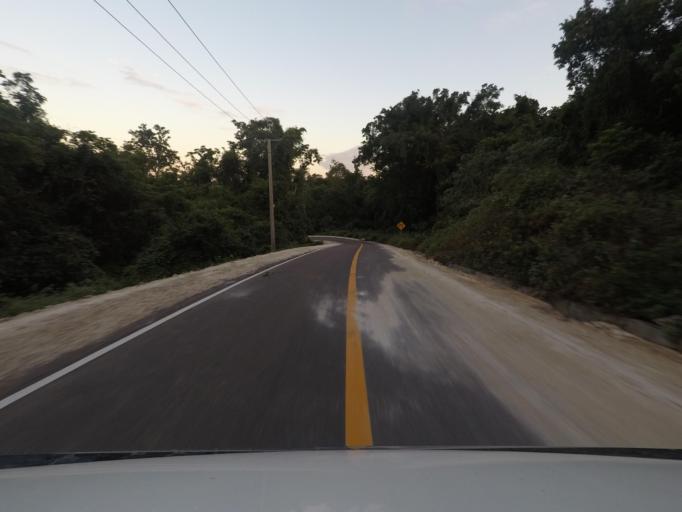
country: TL
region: Lautem
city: Lospalos
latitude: -8.4142
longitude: 127.2936
